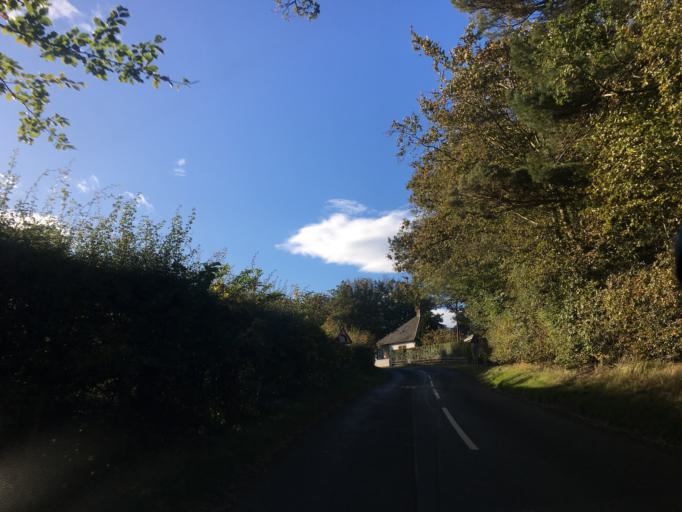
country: GB
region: Scotland
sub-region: East Lothian
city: Pencaitland
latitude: 55.8662
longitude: -2.8834
